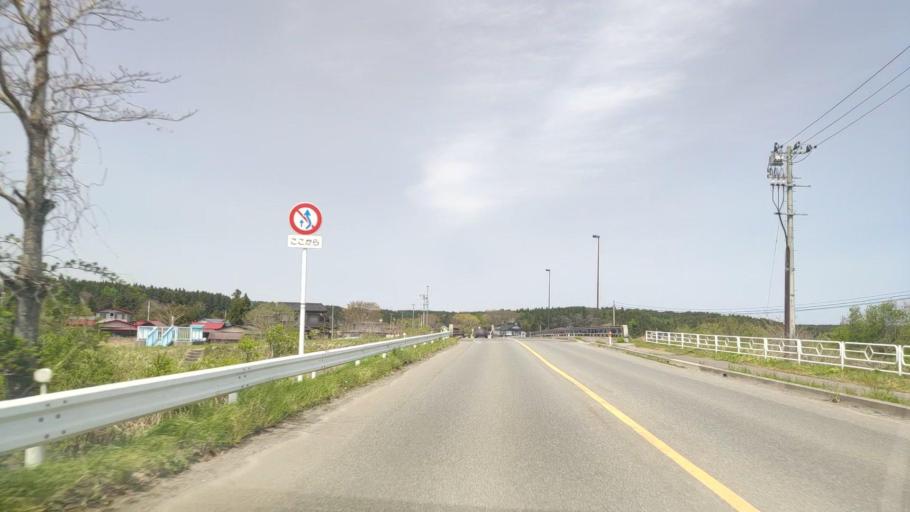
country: JP
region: Aomori
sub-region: Misawa Shi
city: Inuotose
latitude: 40.5560
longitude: 141.3886
